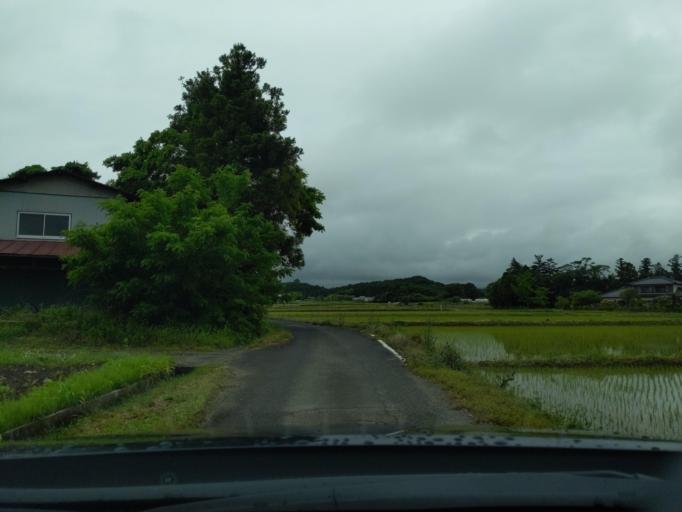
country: JP
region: Fukushima
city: Koriyama
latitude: 37.3714
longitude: 140.2994
